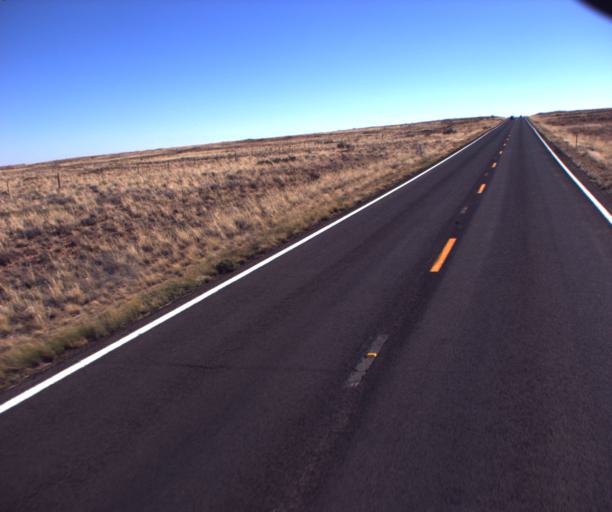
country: US
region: Arizona
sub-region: Coconino County
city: Tuba City
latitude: 35.9747
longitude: -110.9731
